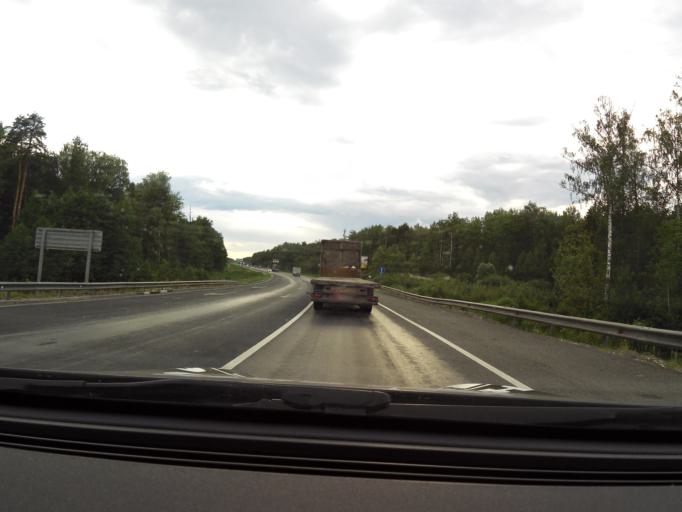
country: RU
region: Vladimir
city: Raduzhnyy
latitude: 56.0649
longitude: 40.3624
